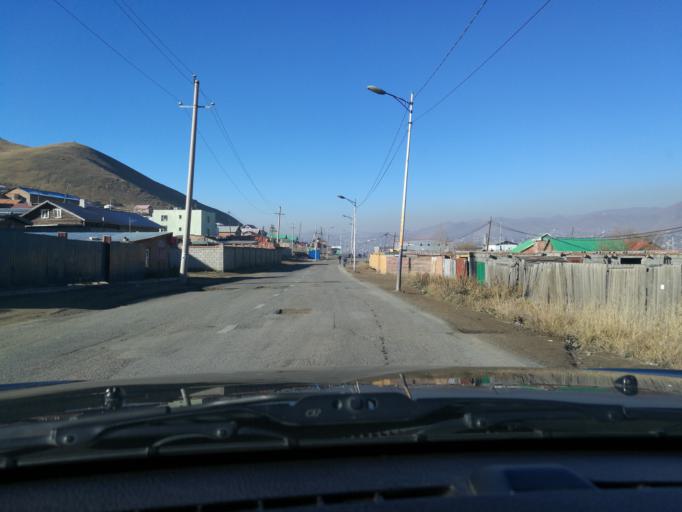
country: MN
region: Ulaanbaatar
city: Ulaanbaatar
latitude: 47.9784
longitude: 106.9409
